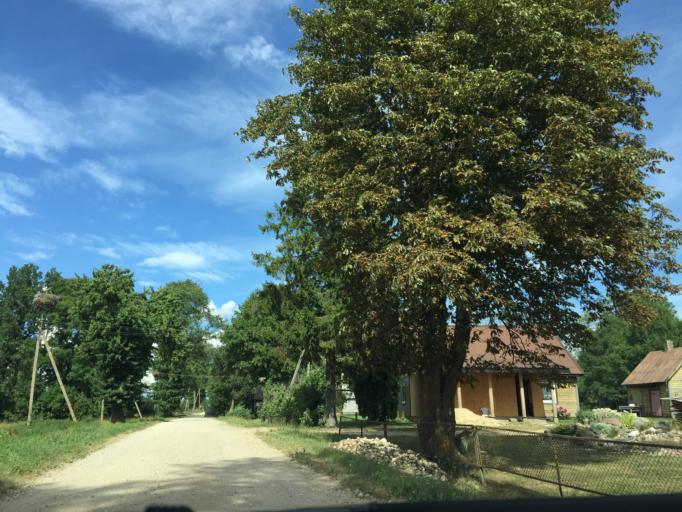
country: LT
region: Siauliu apskritis
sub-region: Joniskis
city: Joniskis
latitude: 56.3452
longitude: 23.6230
